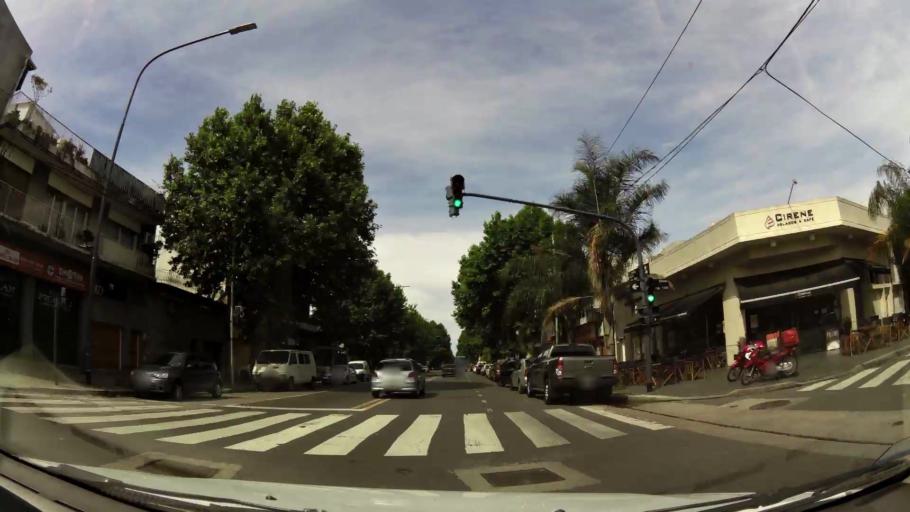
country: AR
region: Buenos Aires F.D.
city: Villa Lugano
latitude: -34.6489
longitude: -58.5088
